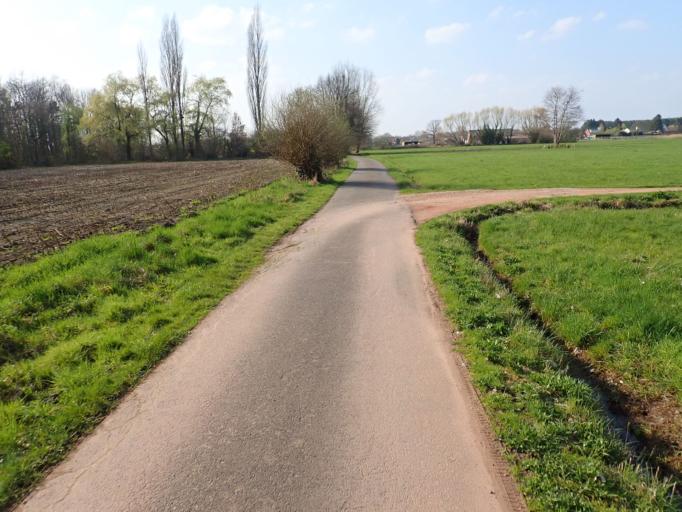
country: BE
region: Flanders
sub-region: Provincie Antwerpen
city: Heist-op-den-Berg
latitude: 51.0380
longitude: 4.7437
